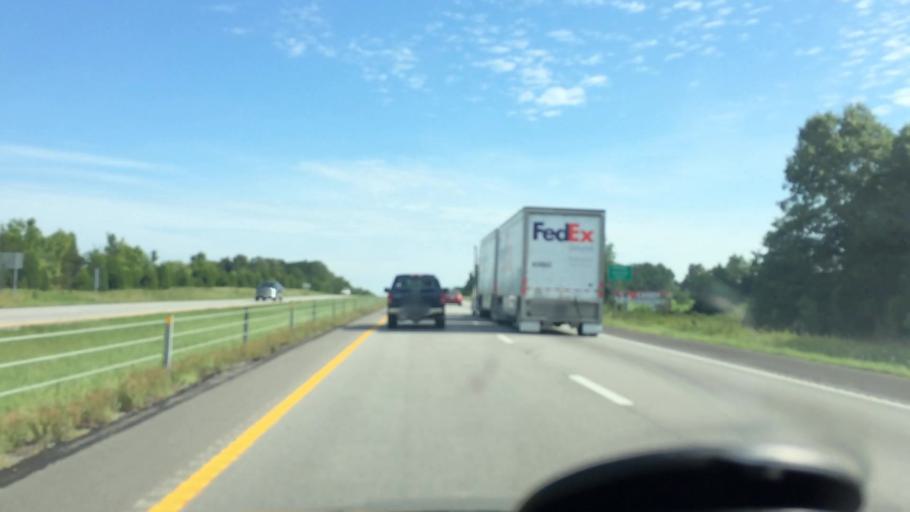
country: US
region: Missouri
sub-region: Webster County
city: Marshfield
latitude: 37.4834
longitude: -92.8523
